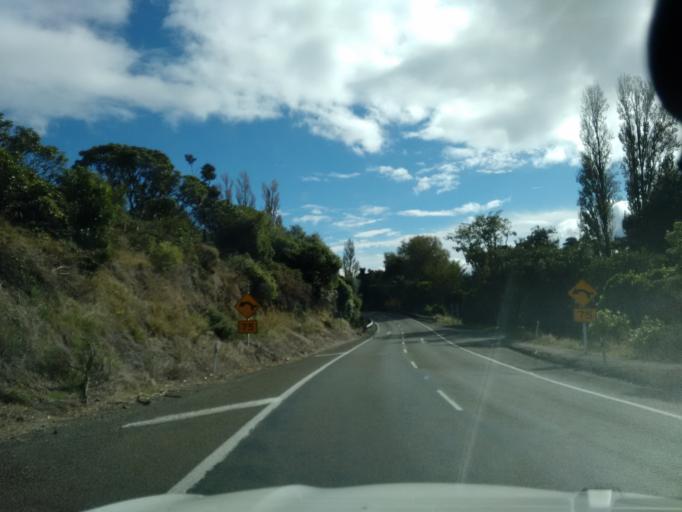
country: NZ
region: Waikato
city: Turangi
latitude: -38.8806
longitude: 175.9735
